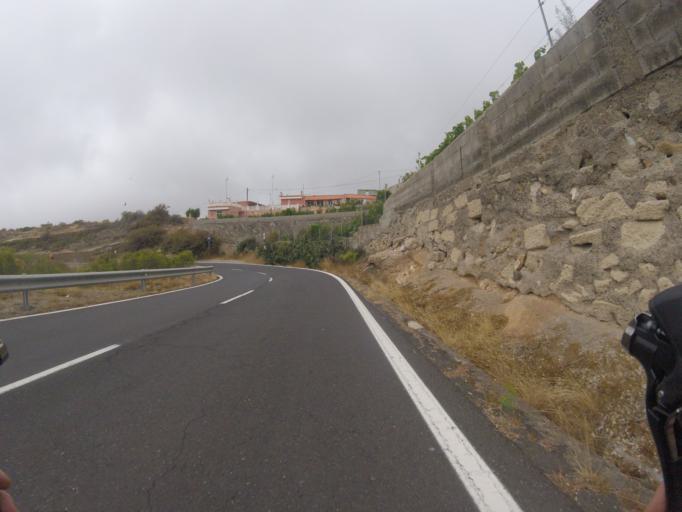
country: ES
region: Canary Islands
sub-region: Provincia de Santa Cruz de Tenerife
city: Fasnia
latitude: 28.2222
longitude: -16.4492
